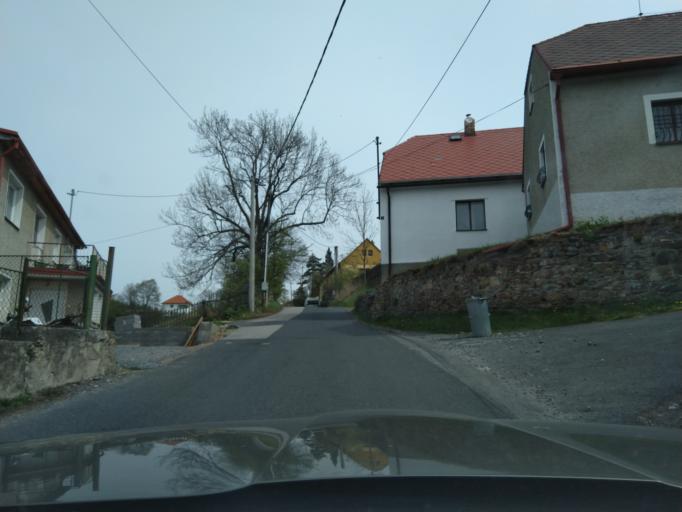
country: CZ
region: Jihocesky
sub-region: Okres Prachatice
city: Stachy
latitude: 49.1804
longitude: 13.6420
